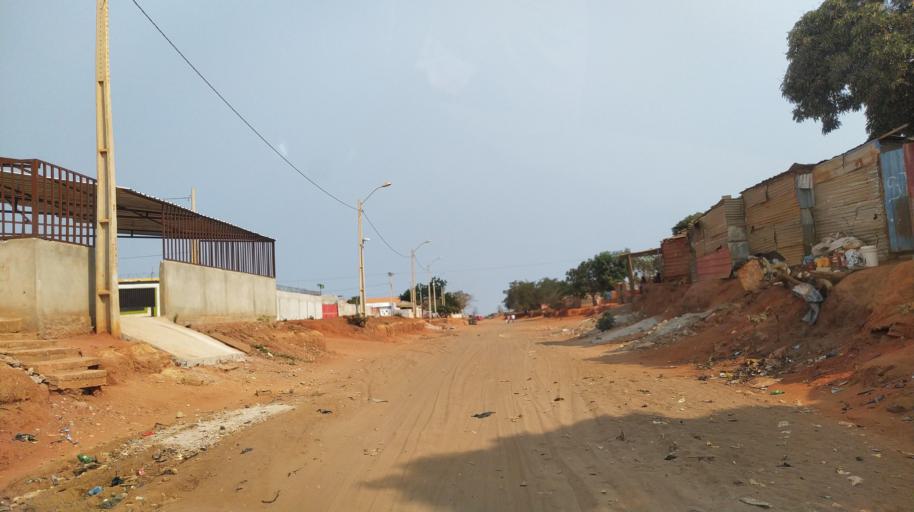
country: AO
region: Luanda
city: Luanda
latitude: -9.0649
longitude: 13.4166
